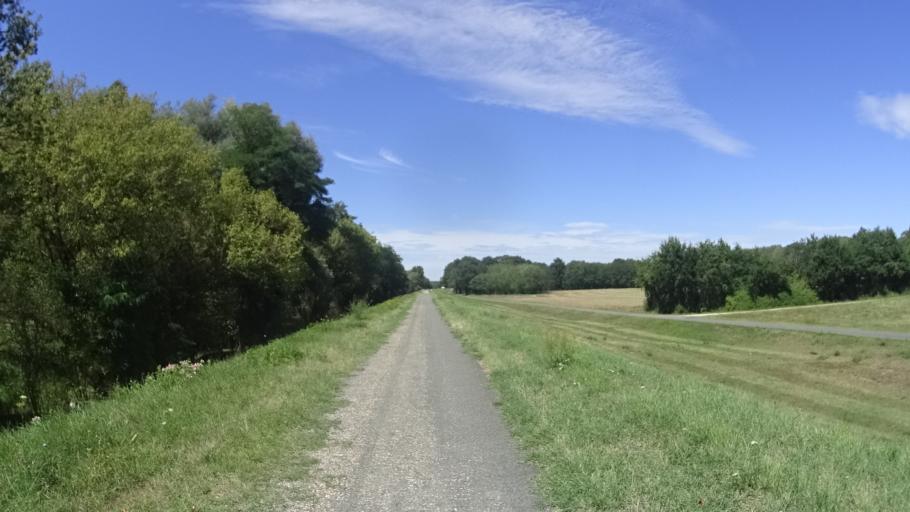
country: FR
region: Centre
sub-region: Departement du Loiret
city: Briare
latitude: 47.5921
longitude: 2.7755
